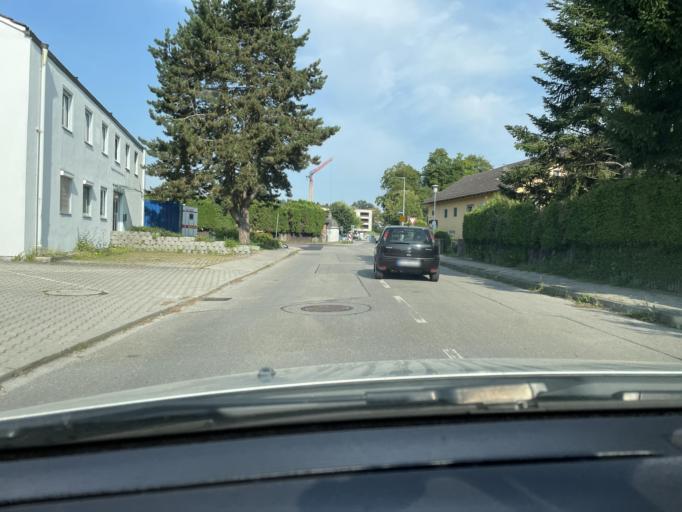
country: DE
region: Bavaria
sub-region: Upper Bavaria
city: Muehldorf
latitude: 48.2421
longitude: 12.5333
